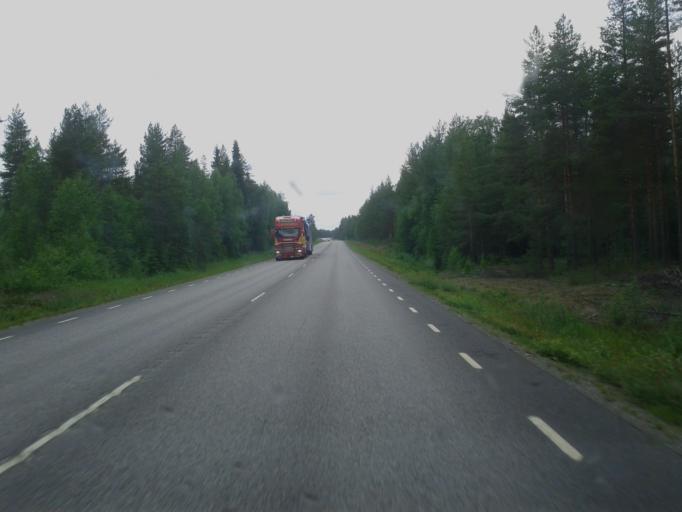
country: SE
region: Vaesterbotten
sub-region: Skelleftea Kommun
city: Langsele
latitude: 64.9428
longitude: 19.9286
